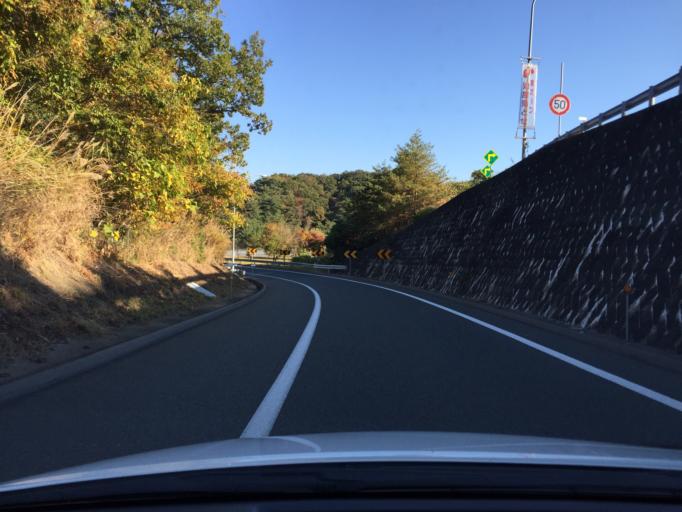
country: JP
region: Fukushima
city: Iwaki
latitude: 37.0389
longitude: 140.8166
